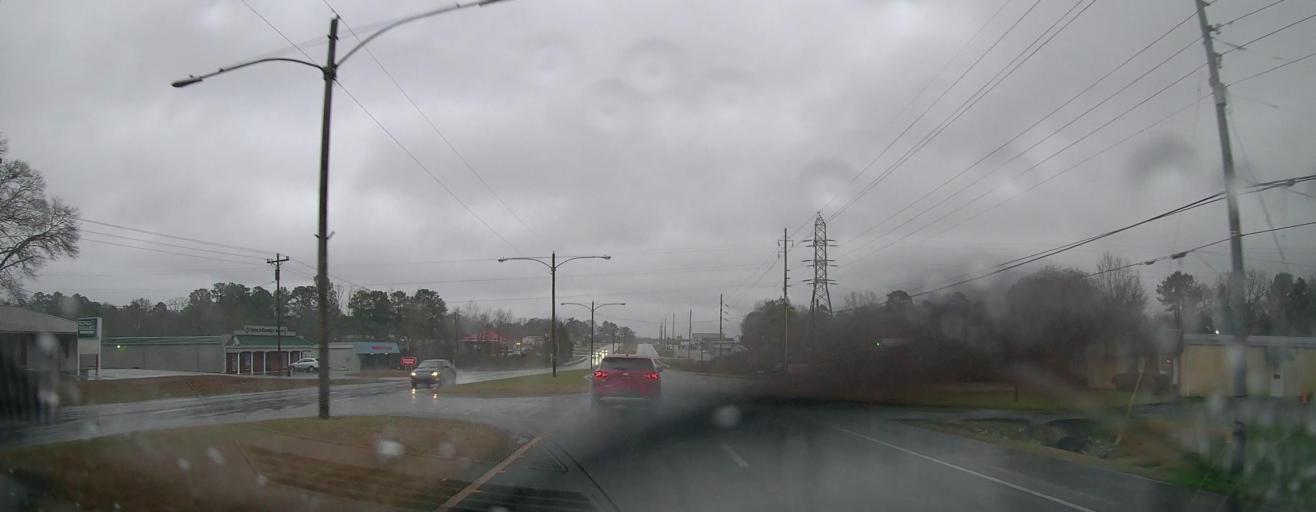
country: US
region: Alabama
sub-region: Morgan County
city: Hartselle
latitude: 34.4280
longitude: -86.9319
